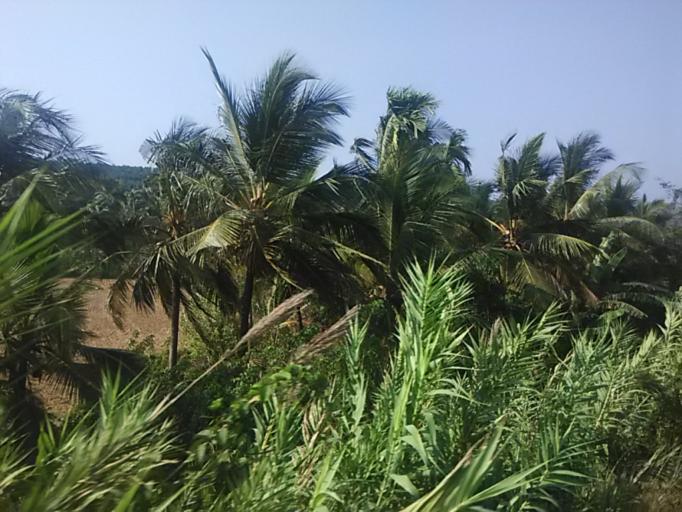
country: IN
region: Kerala
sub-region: Palakkad district
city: Shoranur
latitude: 10.7053
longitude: 76.2675
